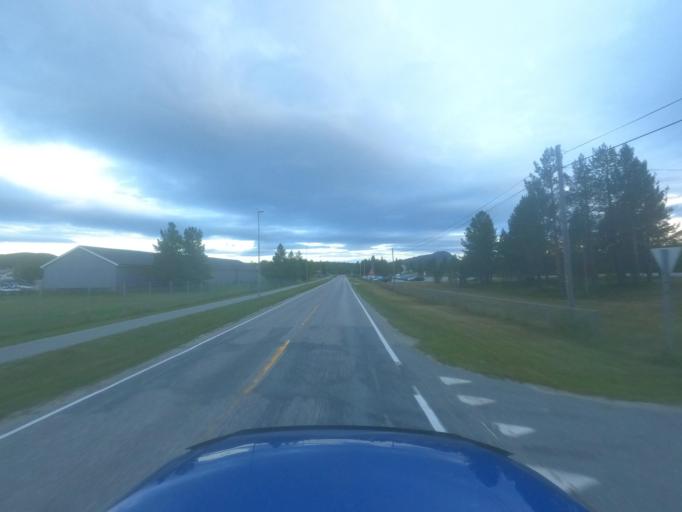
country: NO
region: Finnmark Fylke
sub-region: Porsanger
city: Lakselv
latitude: 69.9049
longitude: 24.9985
